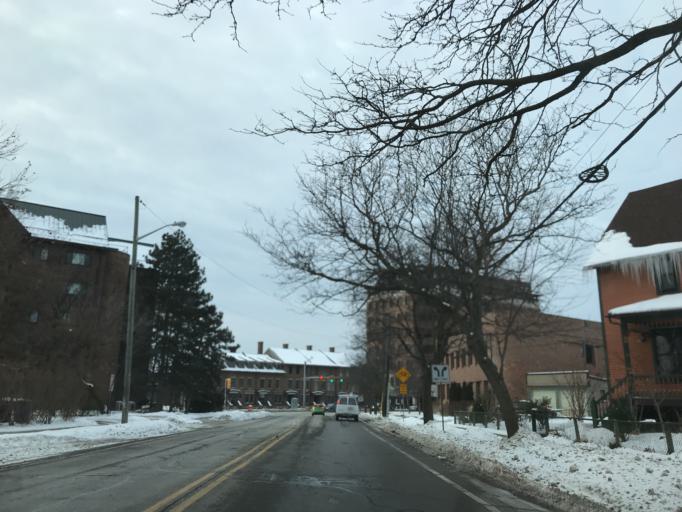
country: US
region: Michigan
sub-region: Washtenaw County
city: Ann Arbor
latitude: 42.2762
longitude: -83.7476
